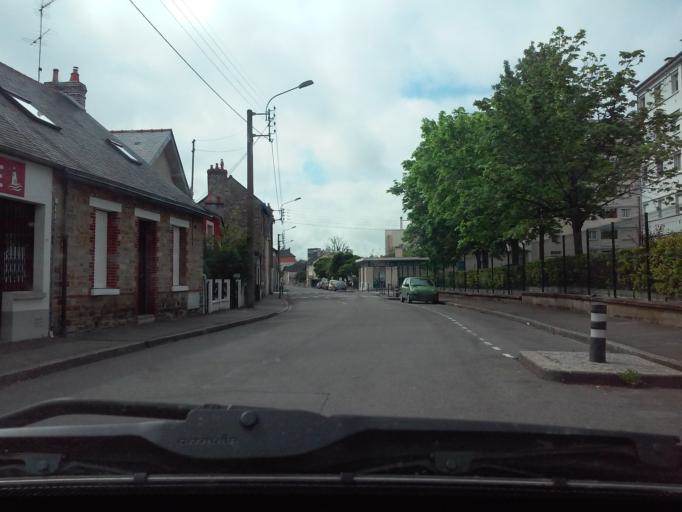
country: FR
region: Brittany
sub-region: Departement d'Ille-et-Vilaine
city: Rennes
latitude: 48.0935
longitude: -1.6858
